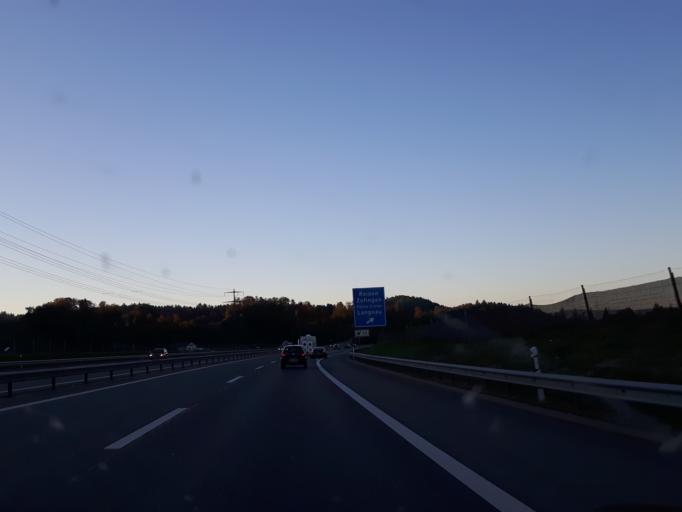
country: CH
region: Lucerne
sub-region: Willisau District
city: Reiden
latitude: 47.2400
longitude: 7.9586
